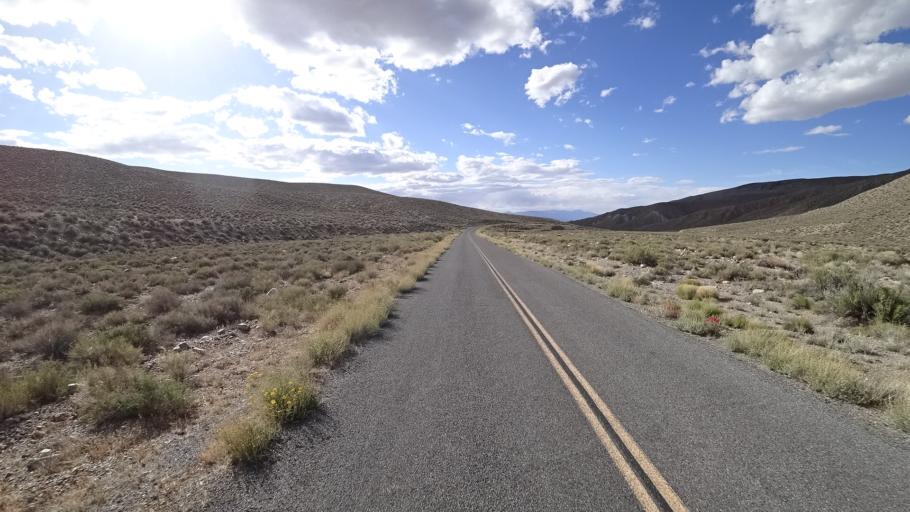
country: US
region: Nevada
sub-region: Nye County
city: Beatty
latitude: 36.3975
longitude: -117.1649
